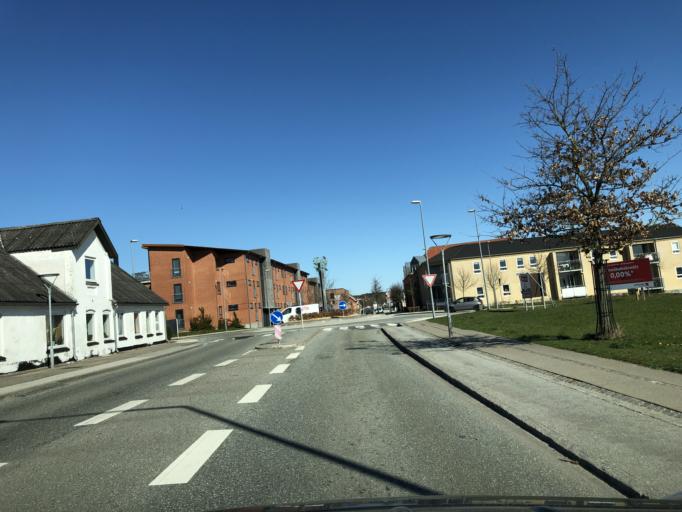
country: DK
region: North Denmark
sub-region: Rebild Kommune
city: Stovring
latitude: 56.8871
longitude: 9.8374
